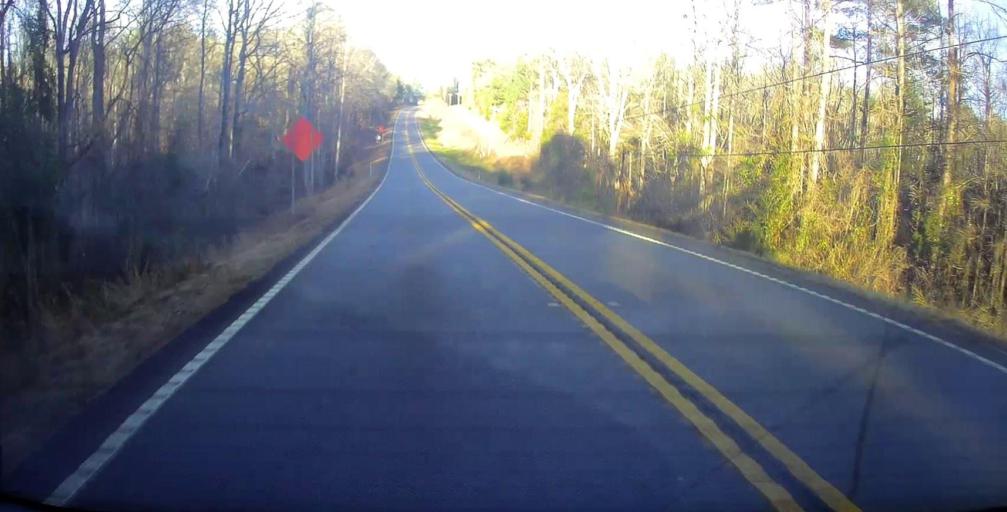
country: US
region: Georgia
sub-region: Upson County
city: Thomaston
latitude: 32.8628
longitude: -84.4092
